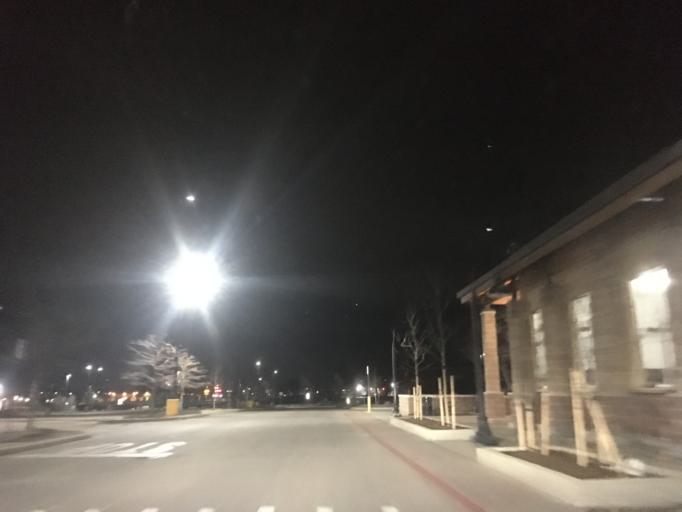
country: US
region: Colorado
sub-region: Boulder County
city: Lafayette
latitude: 40.0056
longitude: -105.1045
